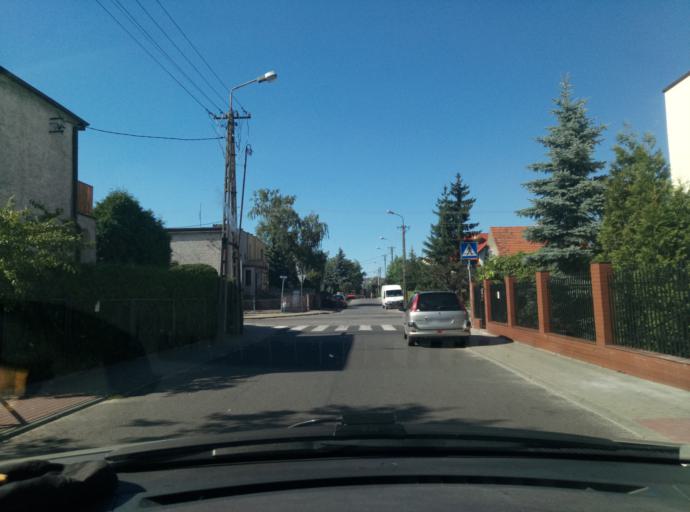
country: PL
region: Kujawsko-Pomorskie
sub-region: Torun
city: Torun
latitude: 53.0473
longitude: 18.5848
